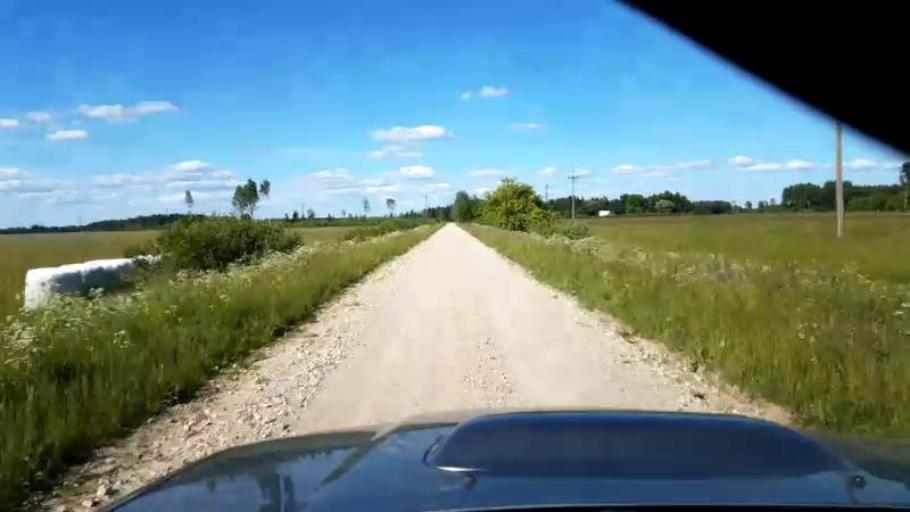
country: EE
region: Paernumaa
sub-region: Sauga vald
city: Sauga
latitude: 58.4988
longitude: 24.5612
